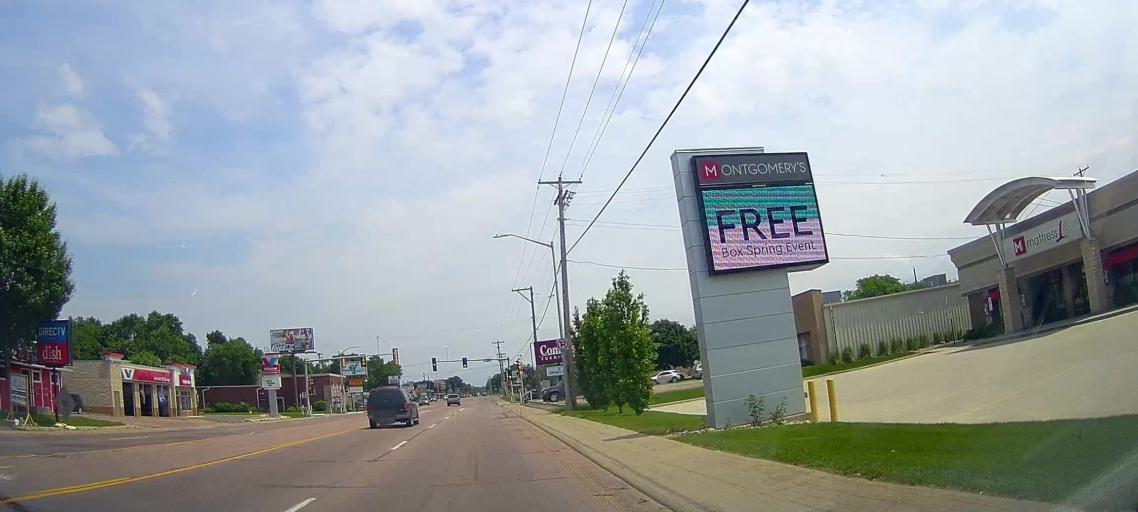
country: US
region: South Dakota
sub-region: Minnehaha County
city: Sioux Falls
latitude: 43.5148
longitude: -96.7470
